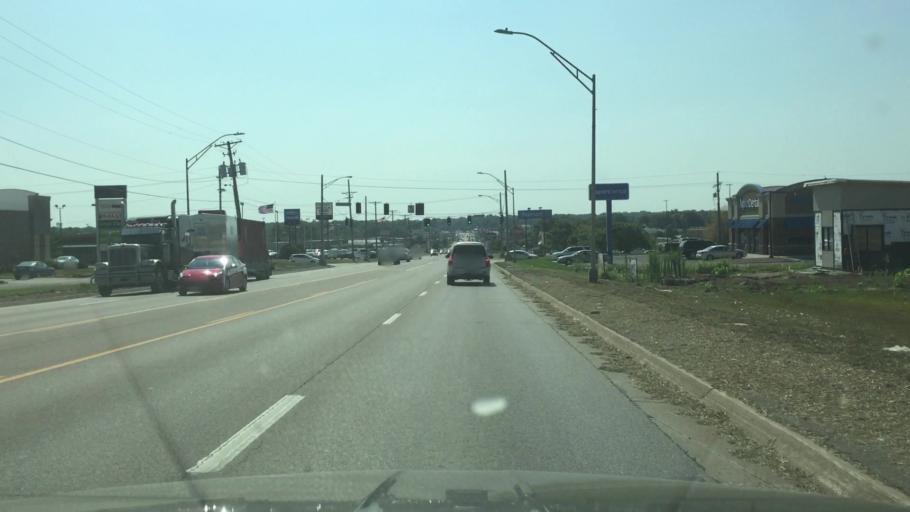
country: US
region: Missouri
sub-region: Pettis County
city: Sedalia
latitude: 38.7107
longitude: -93.2715
